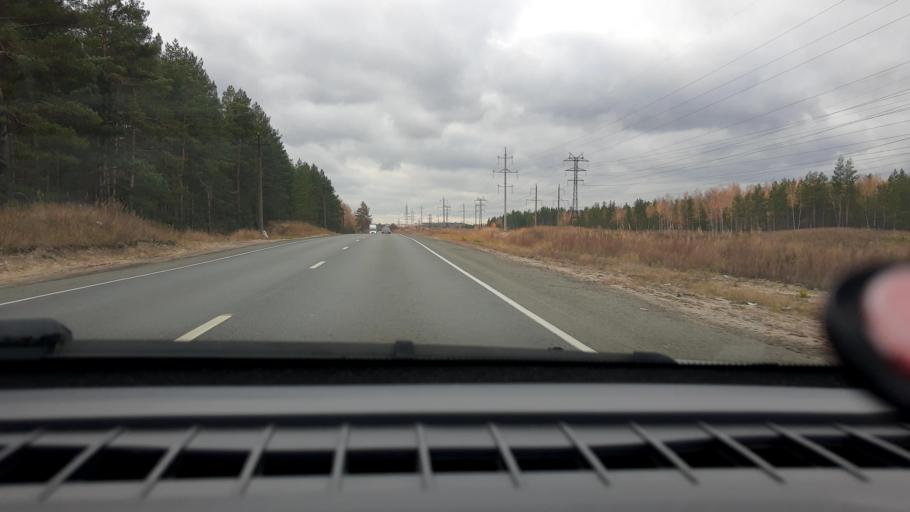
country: RU
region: Nizjnij Novgorod
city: Lukino
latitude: 56.3478
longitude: 43.5855
